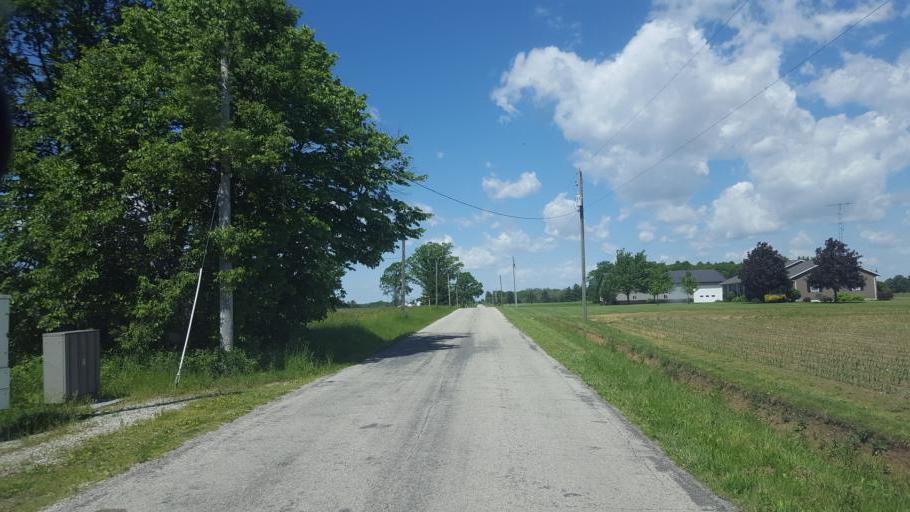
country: US
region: Ohio
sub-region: Richland County
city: Shelby
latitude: 40.8359
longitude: -82.6579
